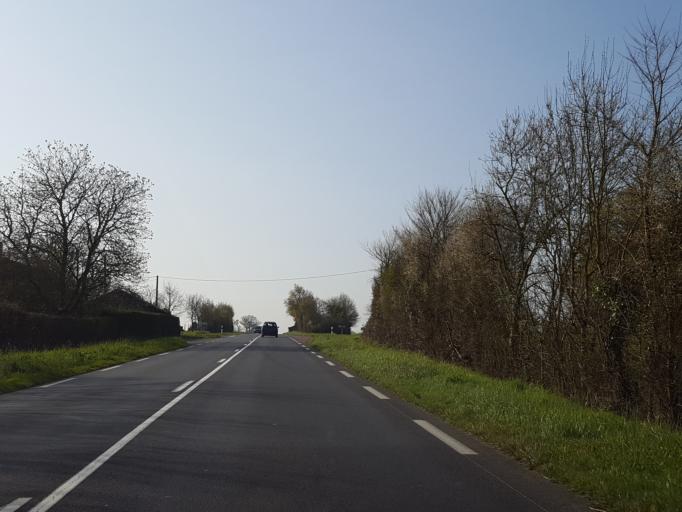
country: FR
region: Pays de la Loire
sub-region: Departement de la Vendee
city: Saint-Philbert-de-Bouaine
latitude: 46.9670
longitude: -1.5164
